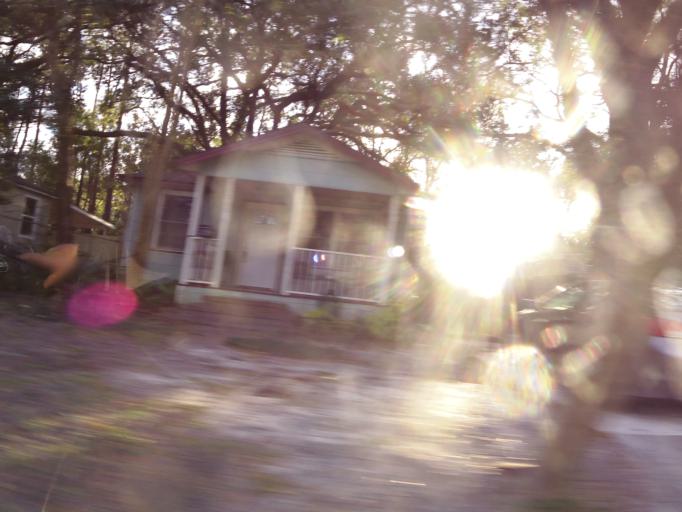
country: US
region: Florida
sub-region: Duval County
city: Jacksonville
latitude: 30.3028
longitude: -81.7154
